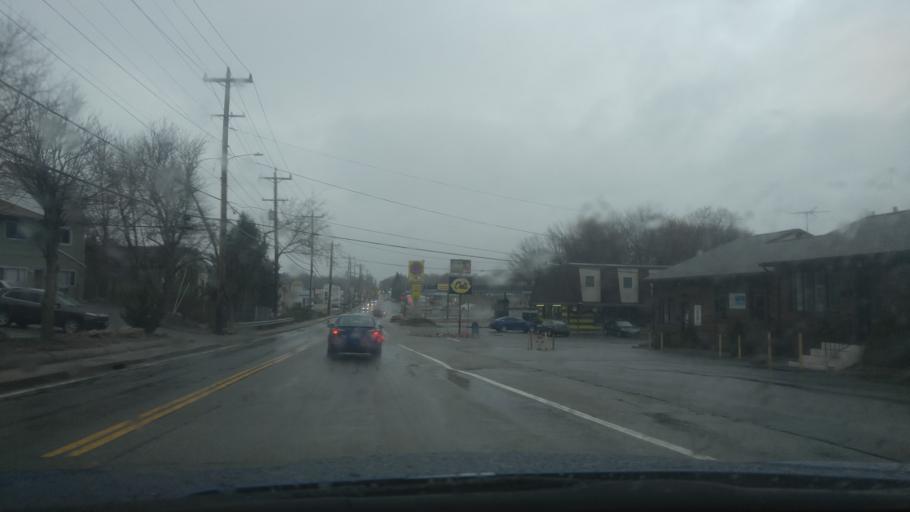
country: US
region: Rhode Island
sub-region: Kent County
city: West Warwick
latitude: 41.6850
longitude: -71.5033
